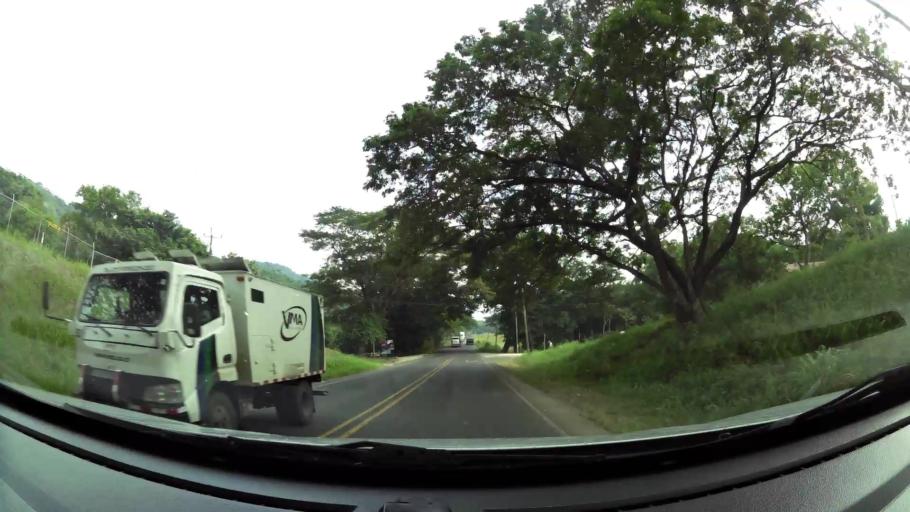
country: CR
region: Guanacaste
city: Juntas
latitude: 10.1963
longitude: -84.9538
